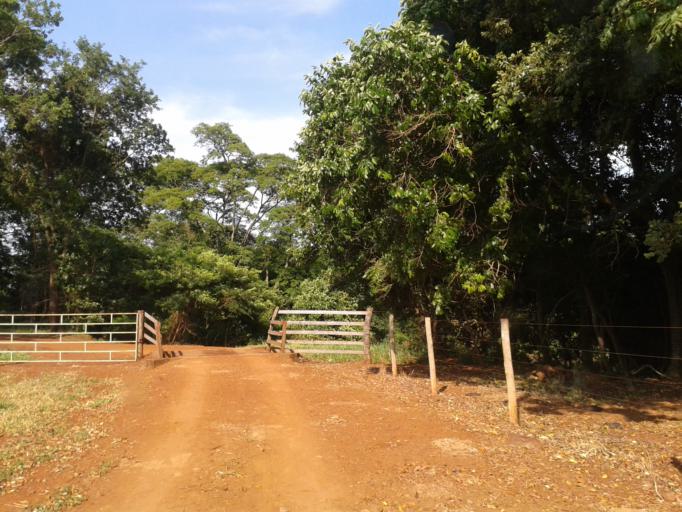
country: BR
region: Minas Gerais
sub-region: Centralina
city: Centralina
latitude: -18.7099
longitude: -49.1948
